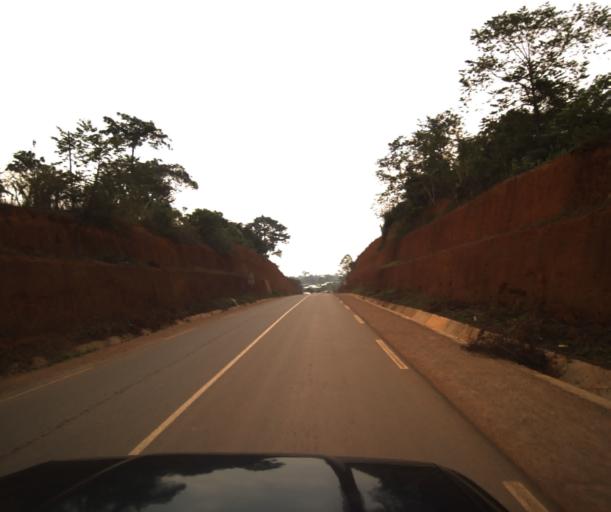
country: CM
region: Centre
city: Mbankomo
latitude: 3.7994
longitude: 11.4519
